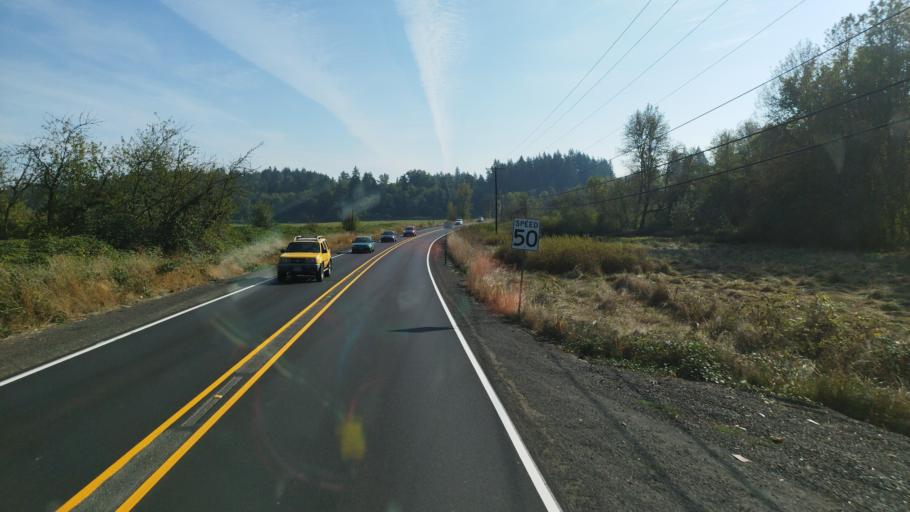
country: US
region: Oregon
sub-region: Washington County
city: Bethany
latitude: 45.5919
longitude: -122.8668
